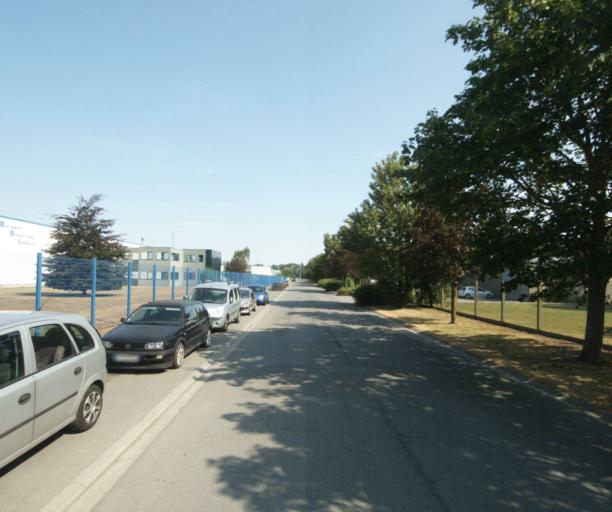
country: FR
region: Nord-Pas-de-Calais
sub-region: Departement du Nord
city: Comines
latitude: 50.7678
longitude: 3.0181
